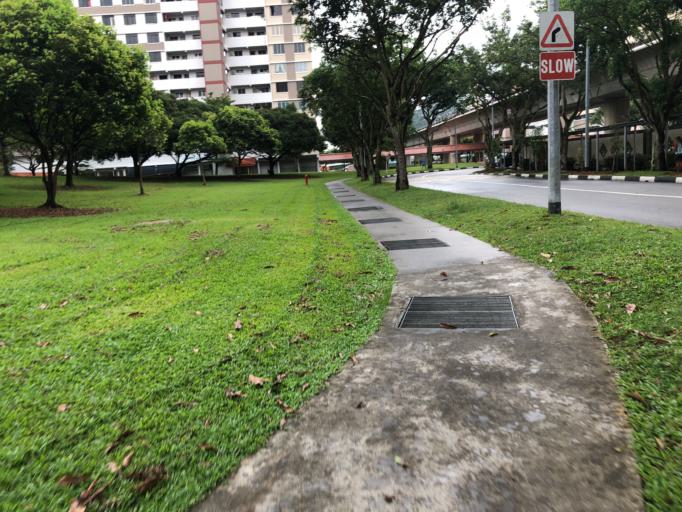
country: MY
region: Johor
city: Johor Bahru
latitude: 1.3558
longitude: 103.7518
